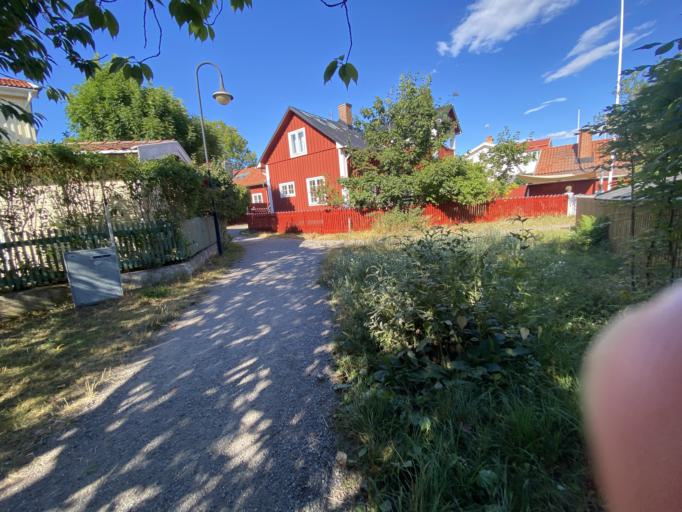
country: SE
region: Stockholm
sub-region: Varmdo Kommun
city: Holo
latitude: 59.2892
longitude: 18.9115
